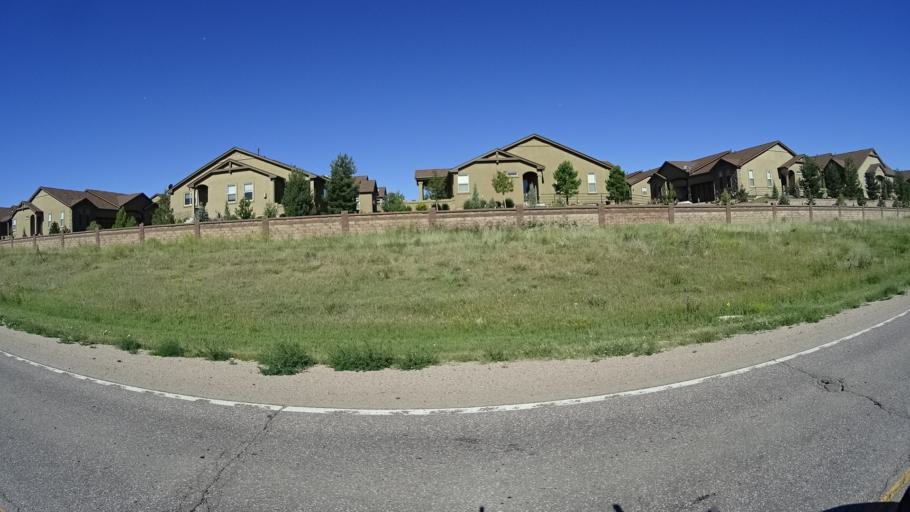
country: US
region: Colorado
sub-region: El Paso County
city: Cimarron Hills
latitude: 38.9235
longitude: -104.6829
